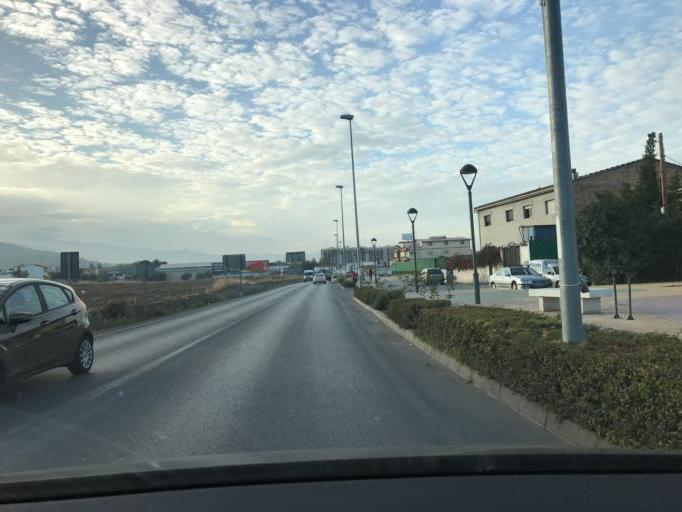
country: ES
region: Andalusia
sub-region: Provincia de Granada
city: Pulianas
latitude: 37.2174
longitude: -3.6097
